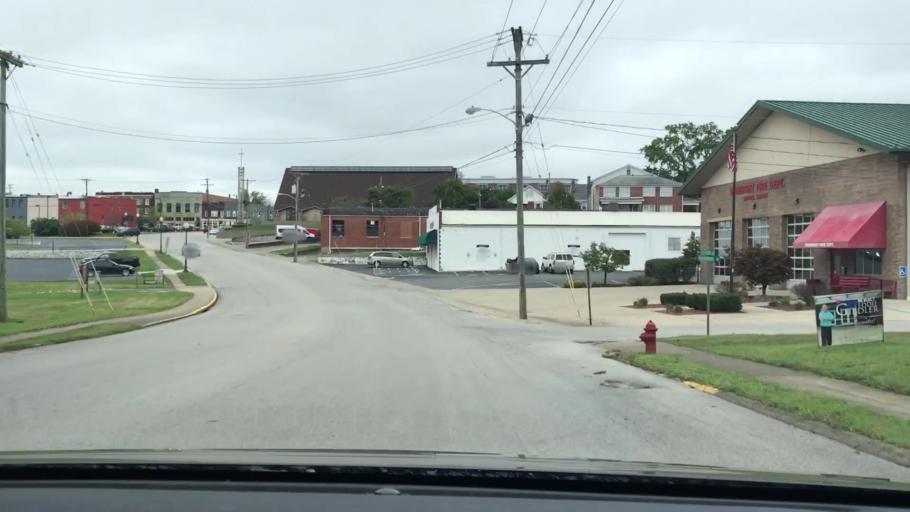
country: US
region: Kentucky
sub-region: Pulaski County
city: Somerset
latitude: 37.0908
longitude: -84.6008
